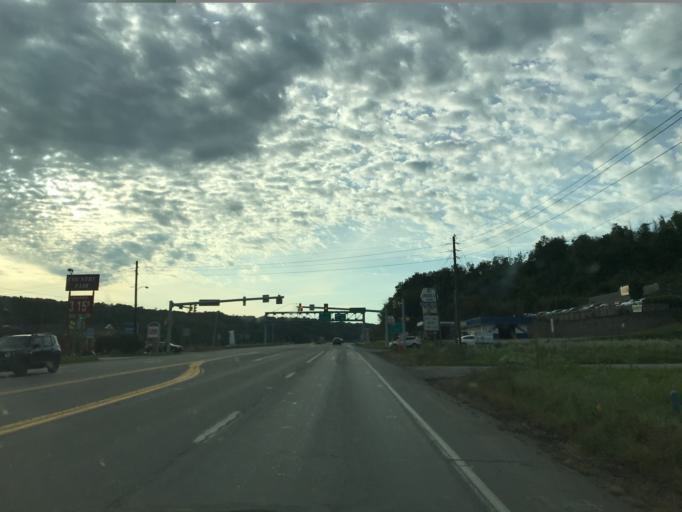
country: US
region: Pennsylvania
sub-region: Crawford County
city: Meadville
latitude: 41.6214
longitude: -80.1728
